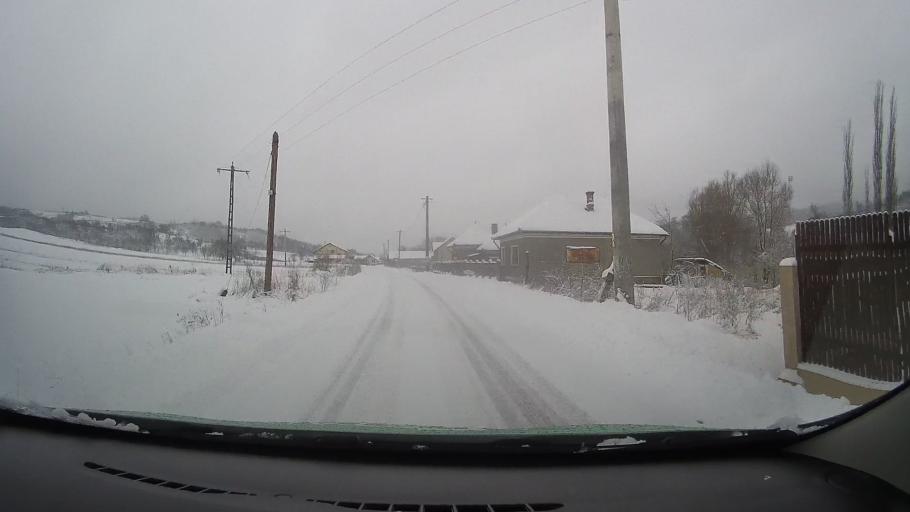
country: RO
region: Hunedoara
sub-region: Comuna Carjiti
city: Carjiti
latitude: 45.8305
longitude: 22.8436
